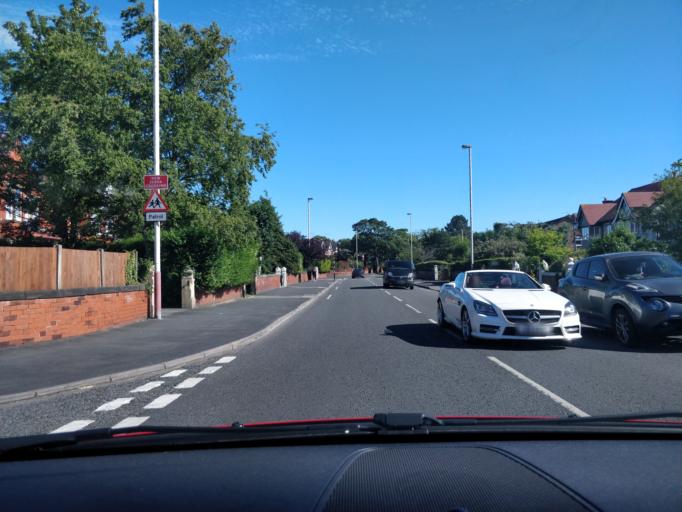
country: GB
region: England
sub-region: Sefton
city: Southport
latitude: 53.6493
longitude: -2.9772
